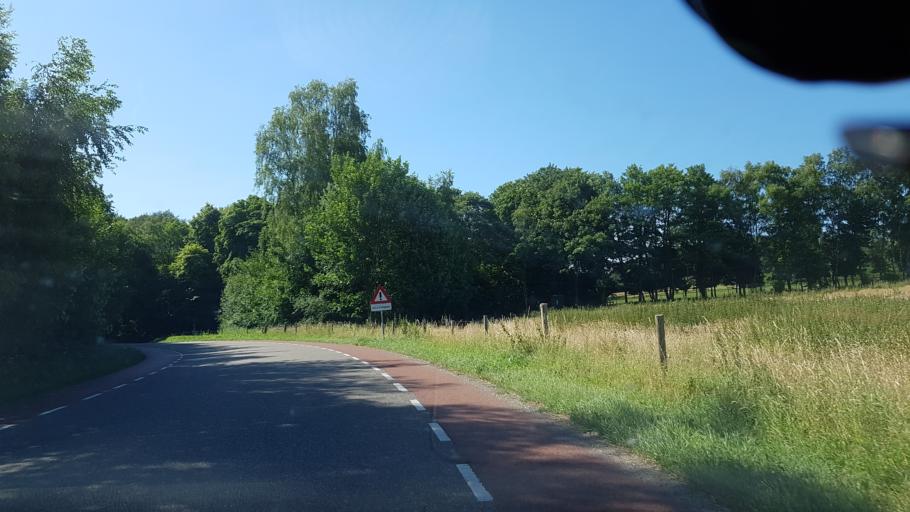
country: NL
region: Gelderland
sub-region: Gemeente Groesbeek
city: Bredeweg
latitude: 51.7425
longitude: 5.9523
